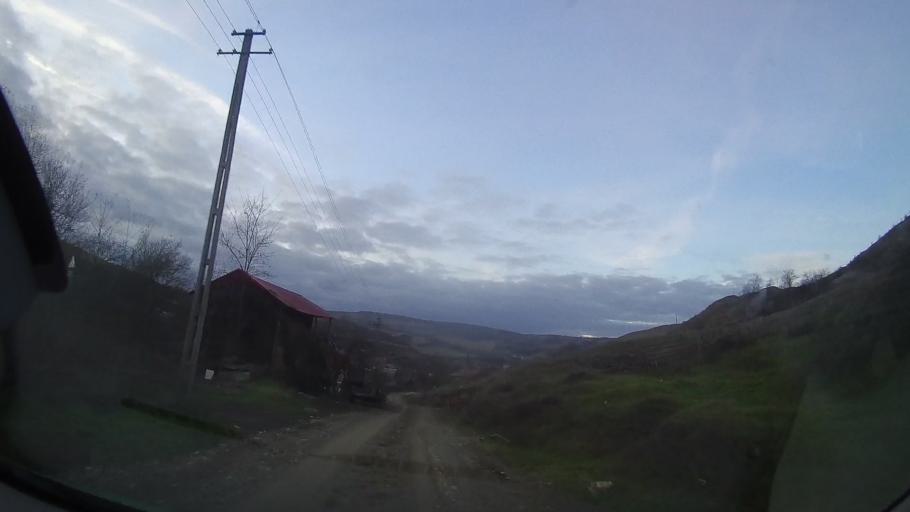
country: RO
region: Cluj
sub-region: Comuna Palatca
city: Palatca
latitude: 46.8639
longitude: 24.0201
